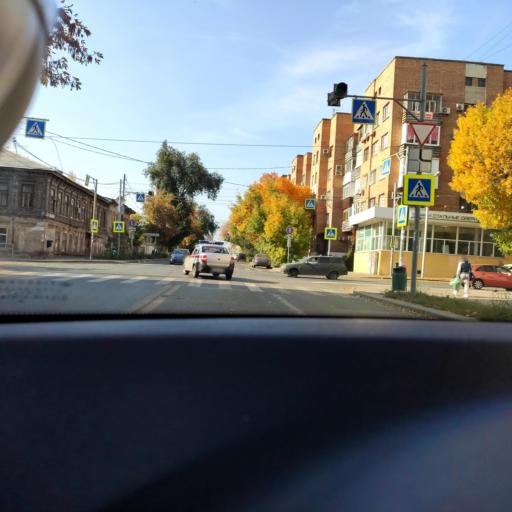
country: RU
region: Samara
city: Samara
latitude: 53.1827
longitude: 50.0990
